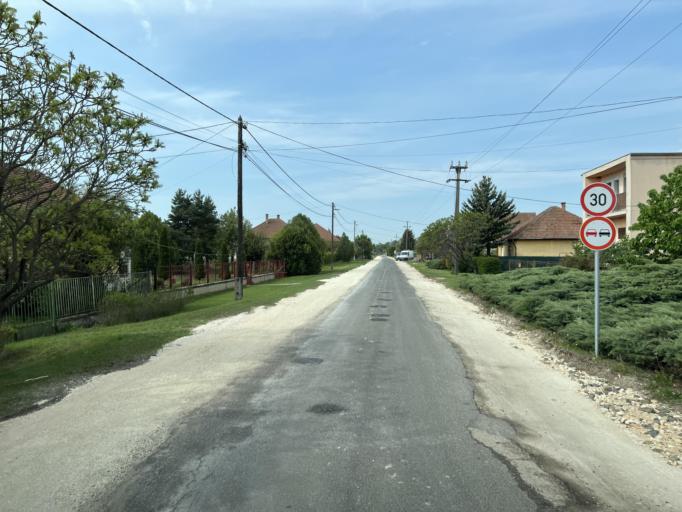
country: HU
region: Pest
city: Tapioszele
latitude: 47.3399
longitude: 19.8824
